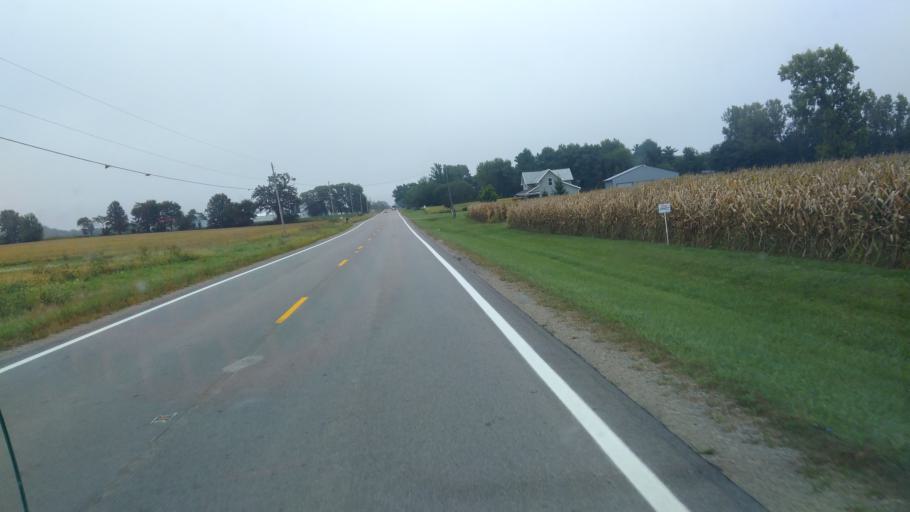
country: US
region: Ohio
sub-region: Union County
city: Richwood
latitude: 40.4788
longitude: -83.4764
